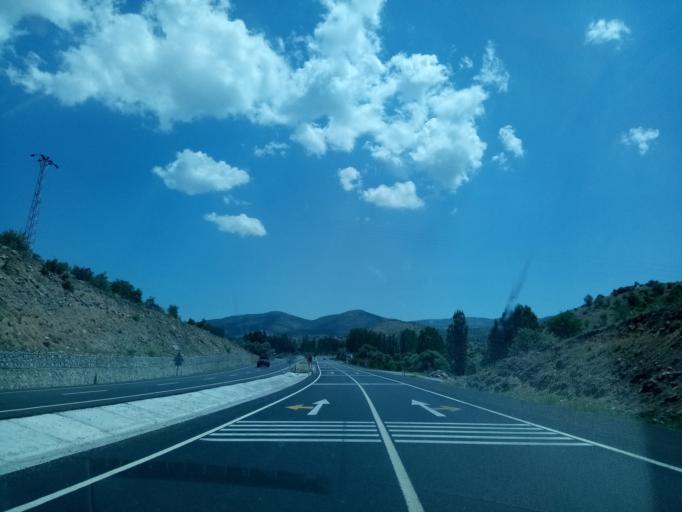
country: TR
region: Konya
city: Cavus
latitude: 37.6599
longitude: 31.9782
